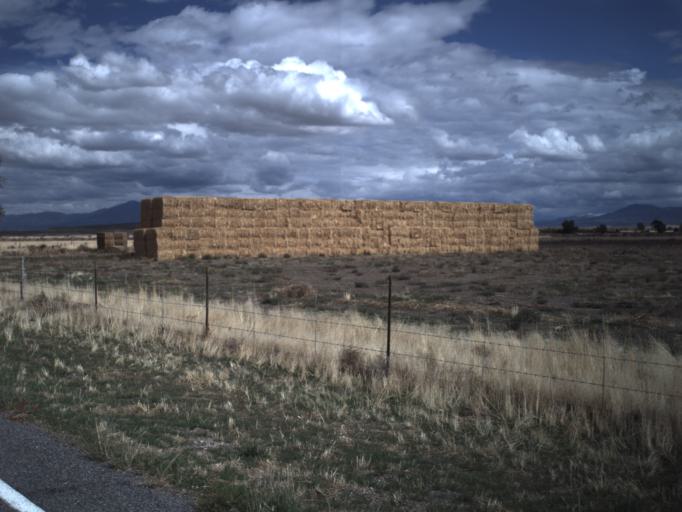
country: US
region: Utah
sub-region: Millard County
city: Fillmore
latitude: 39.0436
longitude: -112.4098
